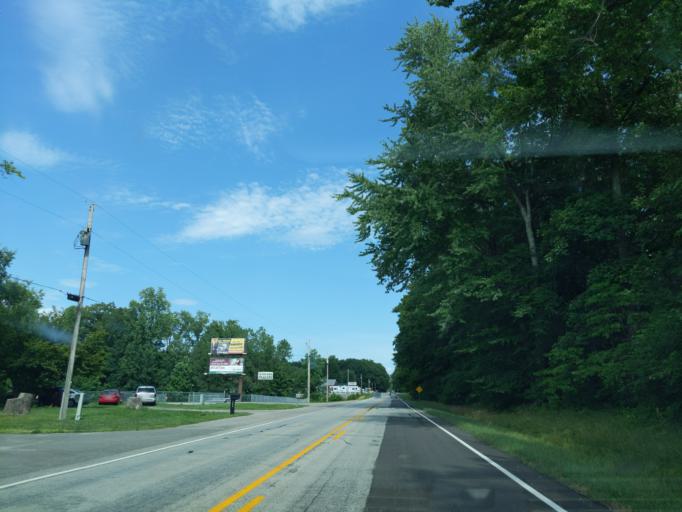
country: US
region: Indiana
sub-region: Ripley County
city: Sunman
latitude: 39.2782
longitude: -85.1318
